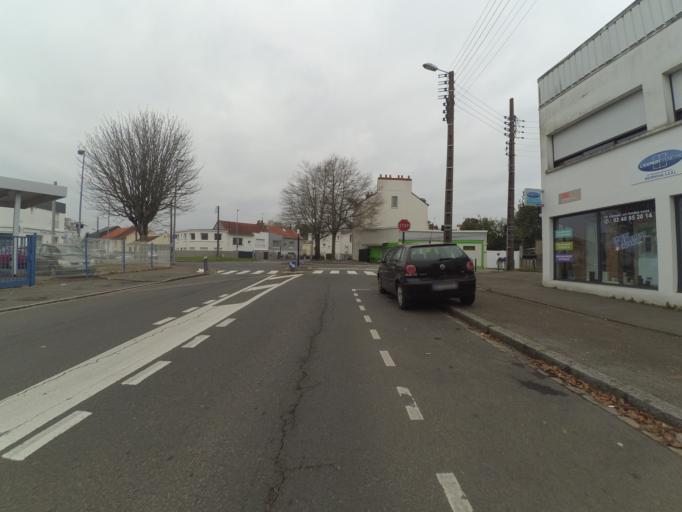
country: FR
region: Pays de la Loire
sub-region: Departement de la Loire-Atlantique
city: Nantes
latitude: 47.2203
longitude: -1.5957
